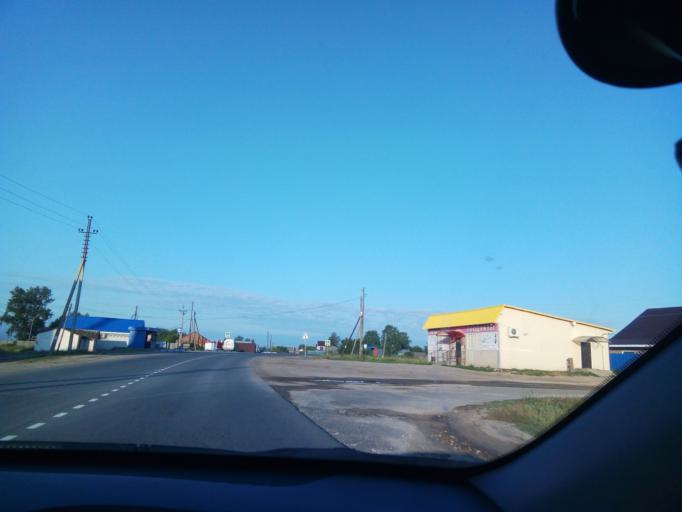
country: RU
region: Nizjnij Novgorod
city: Satis
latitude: 54.9023
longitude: 43.1455
